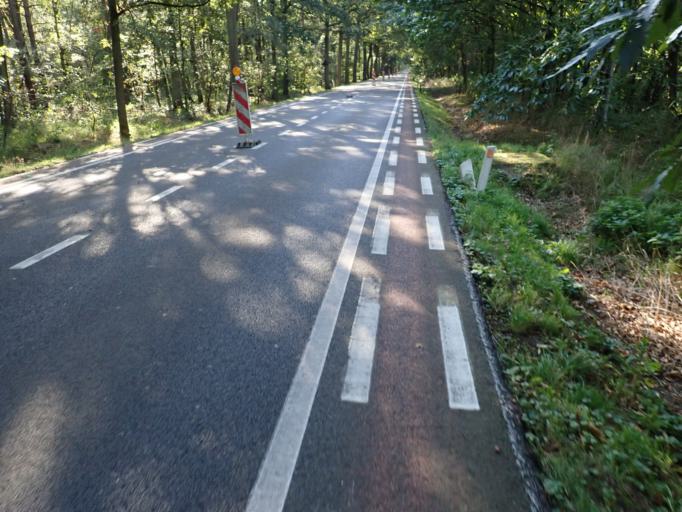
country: BE
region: Flanders
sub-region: Provincie Antwerpen
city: Lille
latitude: 51.2191
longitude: 4.8561
